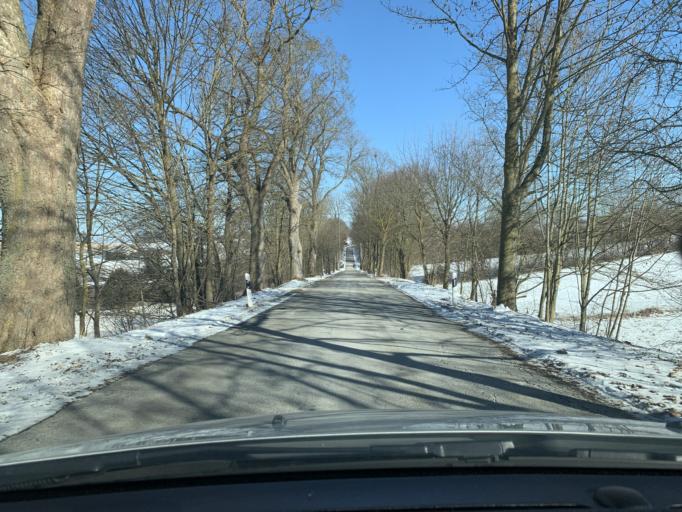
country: DE
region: Bavaria
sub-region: Upper Bavaria
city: Neumarkt-Sankt Veit
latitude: 48.3428
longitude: 12.4946
